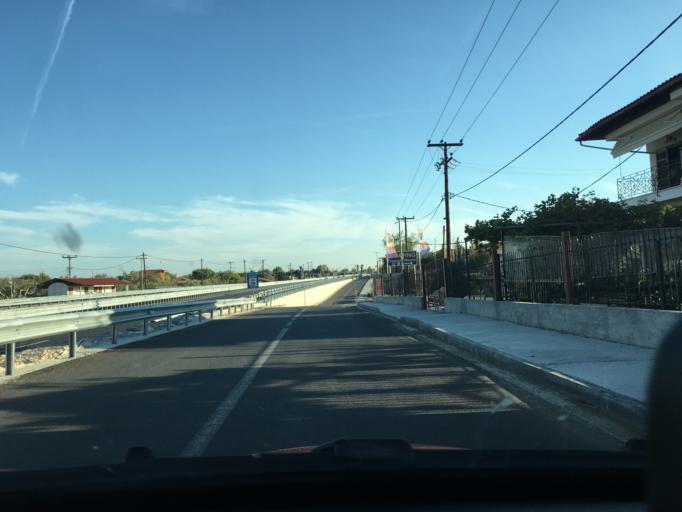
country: GR
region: Central Macedonia
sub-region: Nomos Chalkidikis
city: Nea Potidhaia
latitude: 40.2171
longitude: 23.3201
